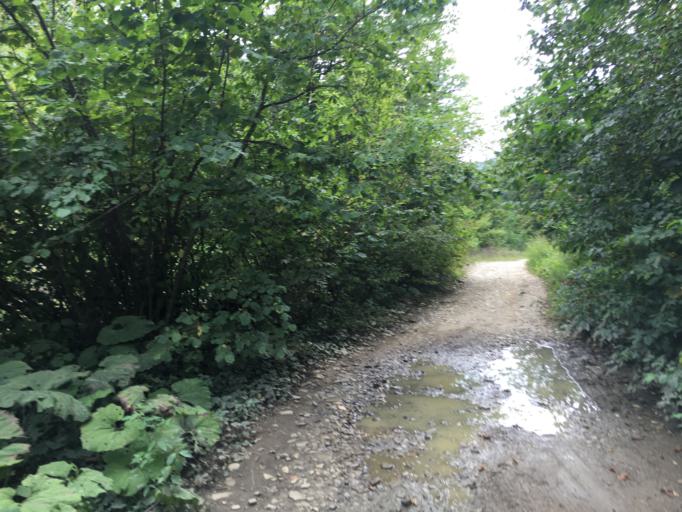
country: RU
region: Krasnodarskiy
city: Tuapse
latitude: 44.2635
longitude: 39.2143
